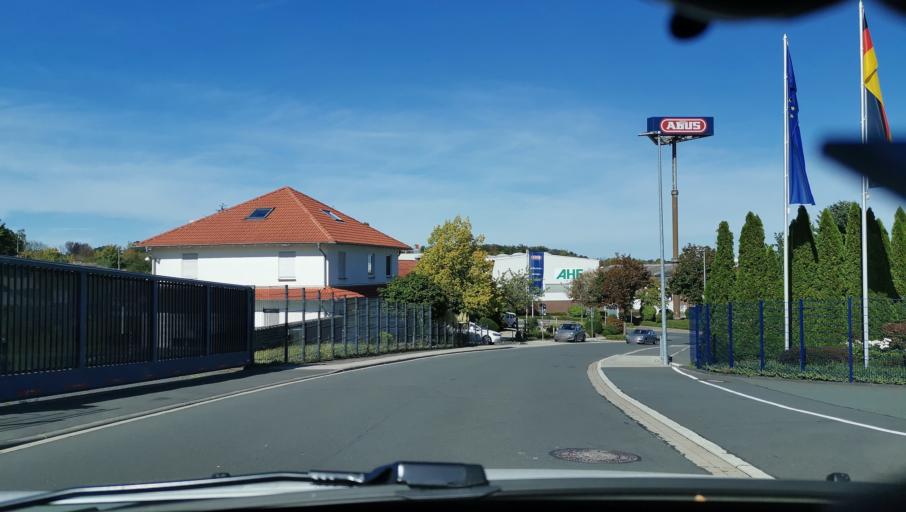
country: DE
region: North Rhine-Westphalia
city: Wetter (Ruhr)
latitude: 51.3574
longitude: 7.3799
